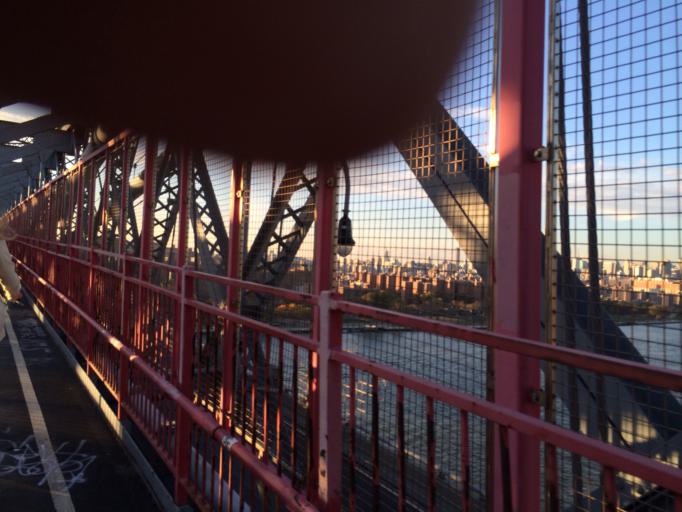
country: US
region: New York
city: New York City
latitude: 40.7133
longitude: -73.9710
